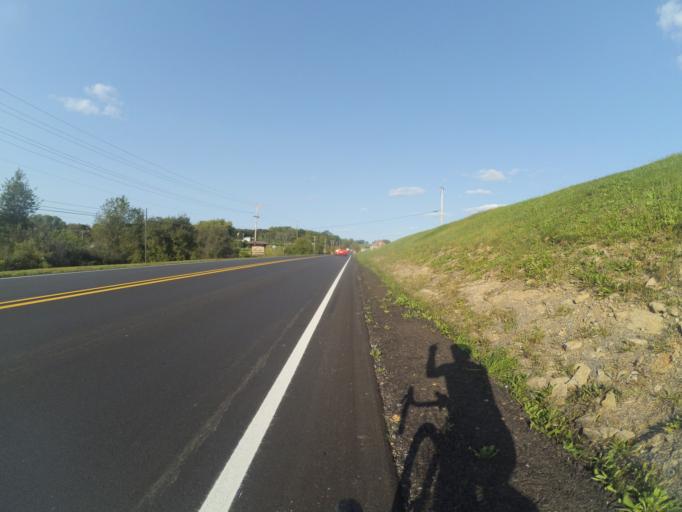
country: US
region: Pennsylvania
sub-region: Centre County
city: Centre Hall
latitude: 40.7975
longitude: -77.7288
